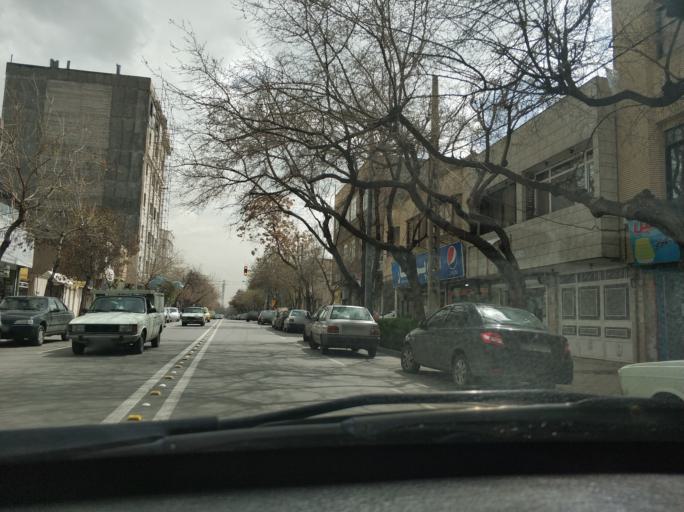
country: IR
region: Razavi Khorasan
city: Mashhad
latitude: 36.2800
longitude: 59.5738
